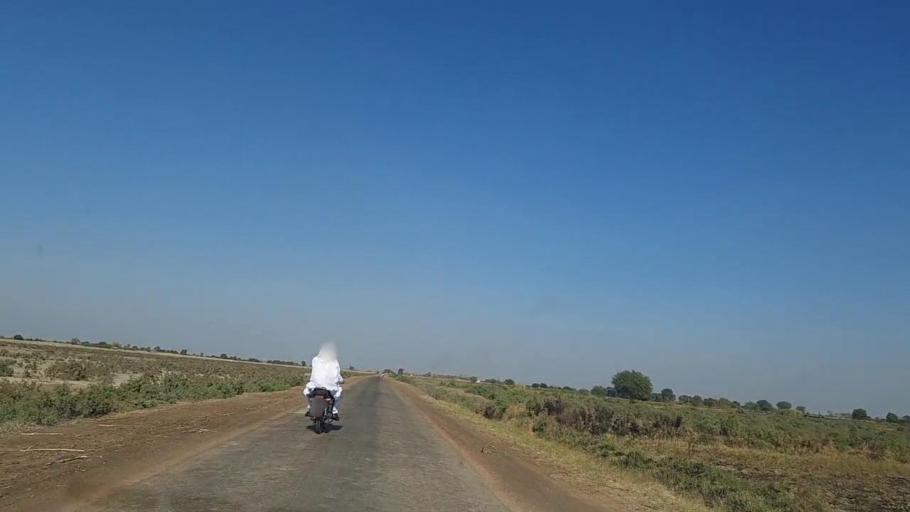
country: PK
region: Sindh
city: Digri
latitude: 25.1470
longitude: 69.0161
